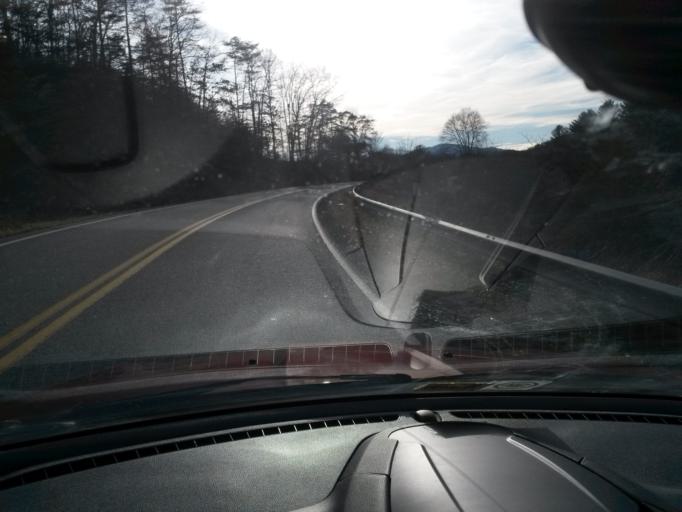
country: US
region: Virginia
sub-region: Alleghany County
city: Clifton Forge
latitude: 37.8494
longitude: -79.7420
